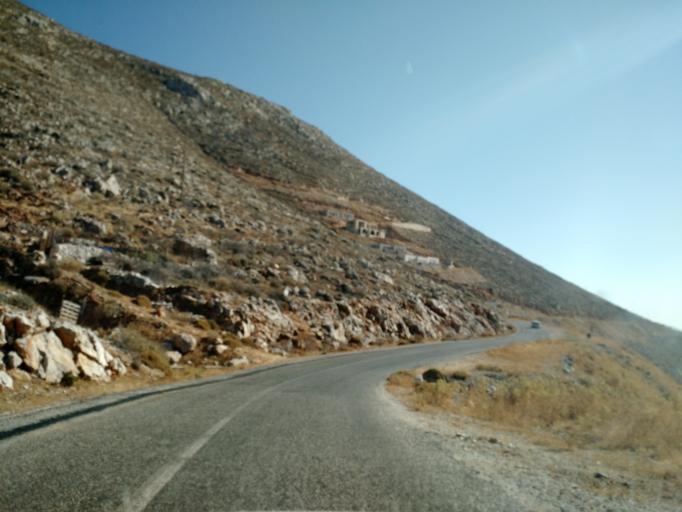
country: GR
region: South Aegean
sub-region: Nomos Kykladon
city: Amorgos
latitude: 36.8936
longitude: 25.9641
